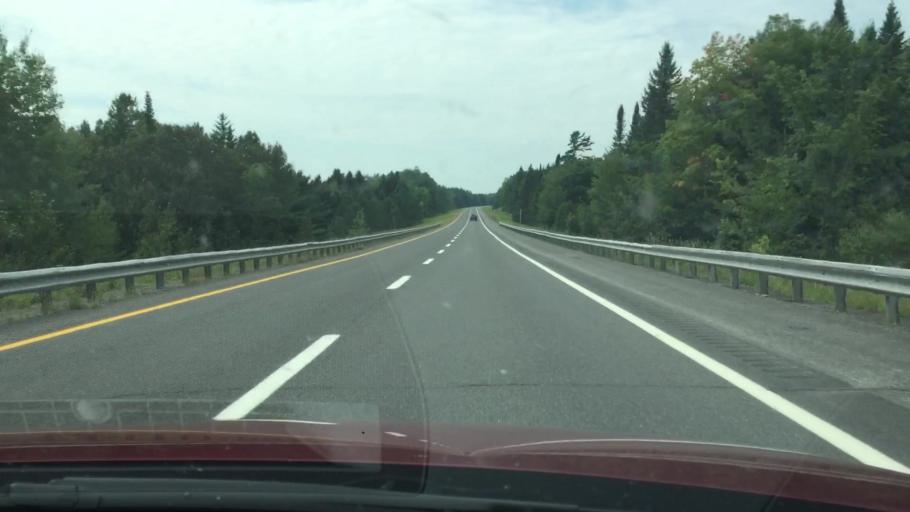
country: US
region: Maine
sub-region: Aroostook County
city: Houlton
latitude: 46.1372
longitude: -67.8944
